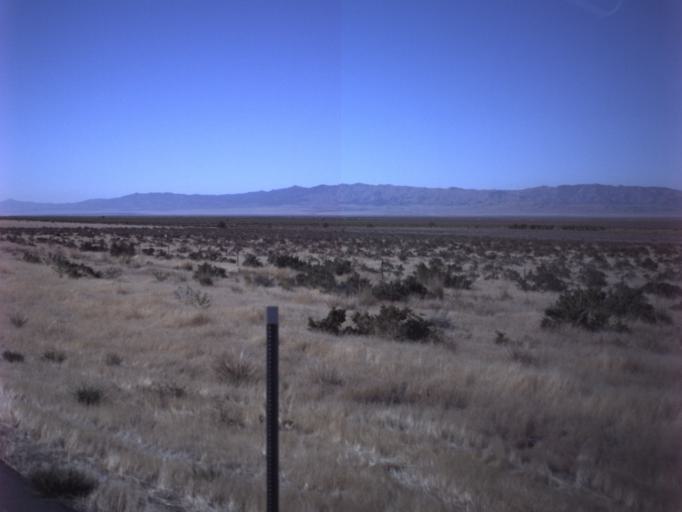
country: US
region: Utah
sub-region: Tooele County
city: Grantsville
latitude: 40.6640
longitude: -112.6772
